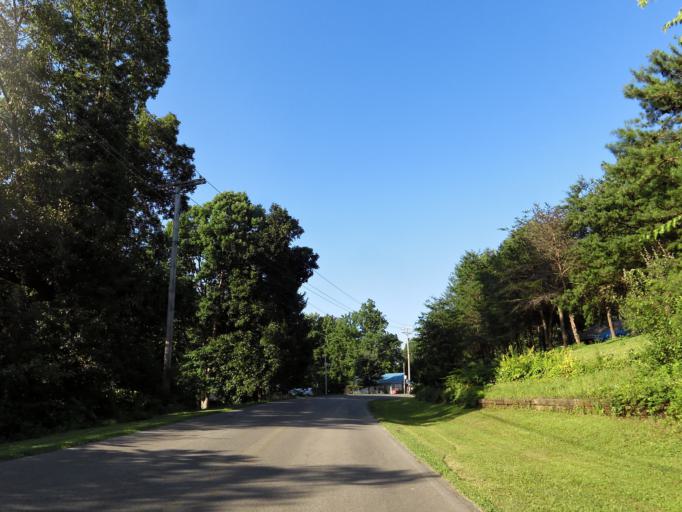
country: US
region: Tennessee
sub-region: Blount County
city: Maryville
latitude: 35.7347
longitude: -83.9124
